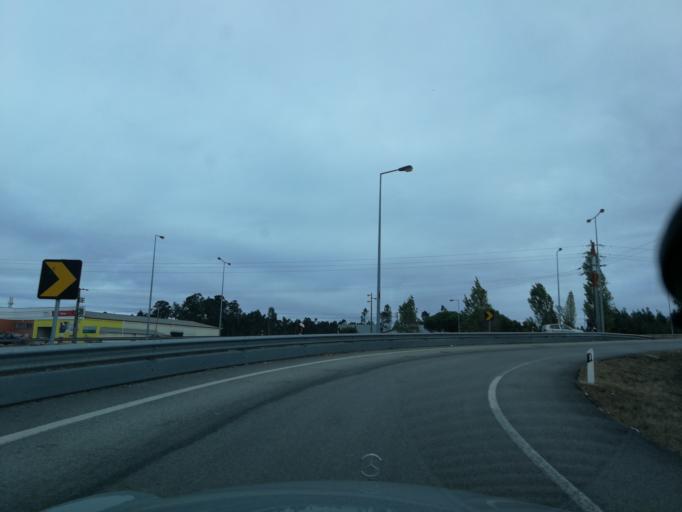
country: PT
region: Aveiro
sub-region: Agueda
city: Valongo
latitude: 40.5941
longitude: -8.4699
